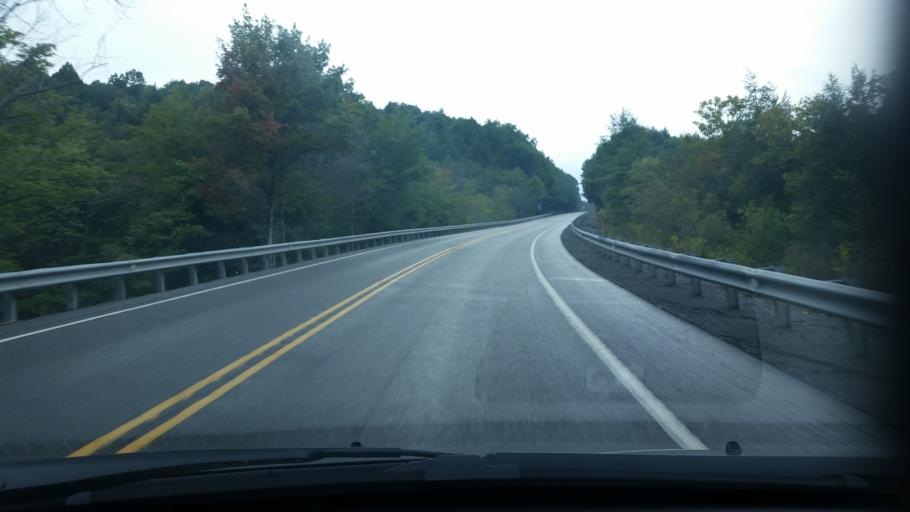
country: US
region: Pennsylvania
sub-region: Clearfield County
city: Shiloh
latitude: 41.0865
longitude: -78.2469
